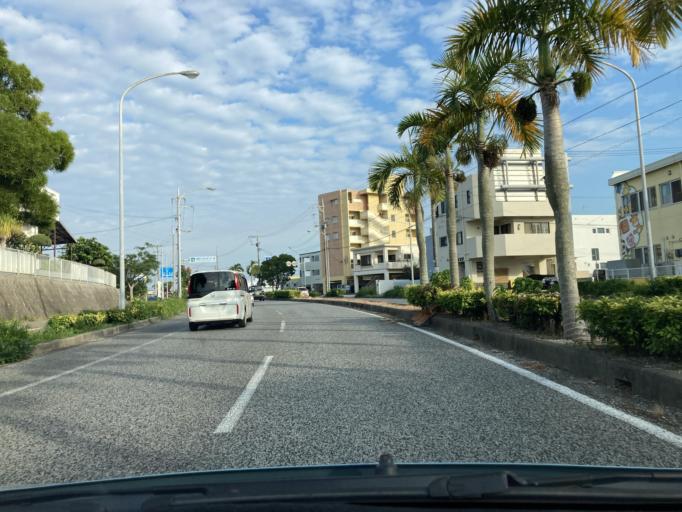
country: JP
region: Okinawa
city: Okinawa
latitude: 26.3519
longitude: 127.8155
